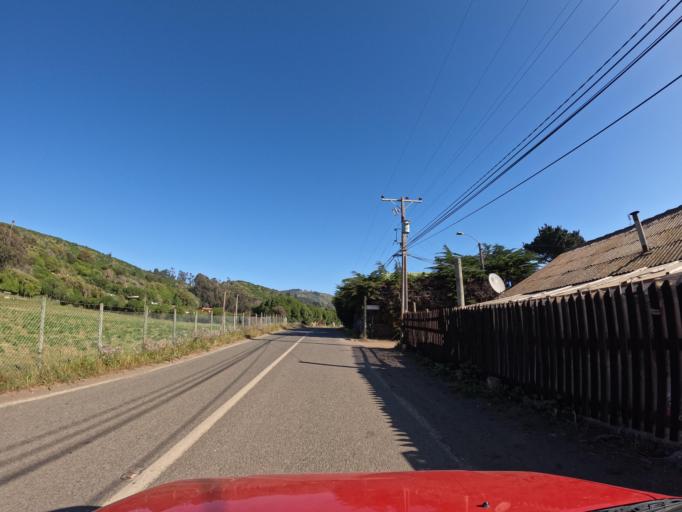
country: CL
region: Maule
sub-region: Provincia de Talca
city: Constitucion
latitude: -34.8432
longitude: -72.1418
